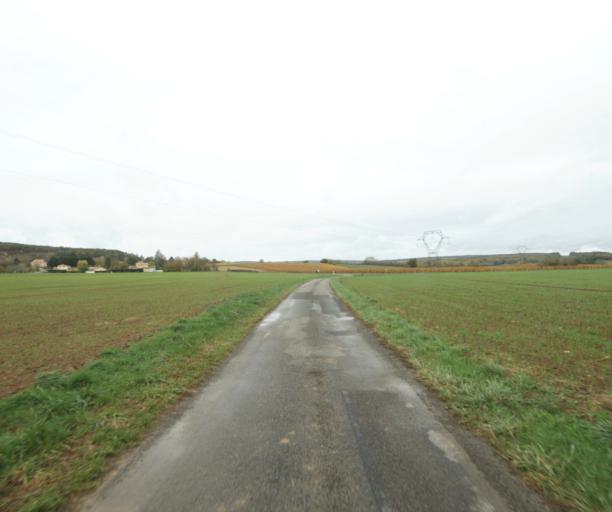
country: FR
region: Bourgogne
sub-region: Departement de Saone-et-Loire
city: Saint-Martin-Belle-Roche
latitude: 46.4688
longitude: 4.8583
